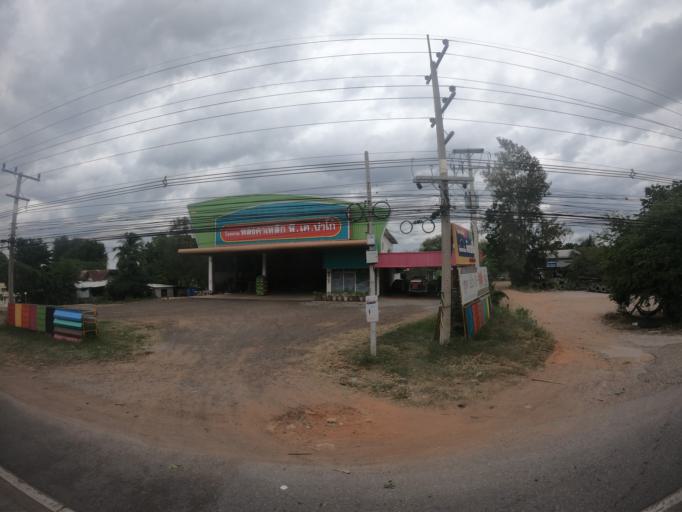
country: TH
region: Nakhon Ratchasima
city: Nakhon Ratchasima
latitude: 14.9069
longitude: 102.1551
